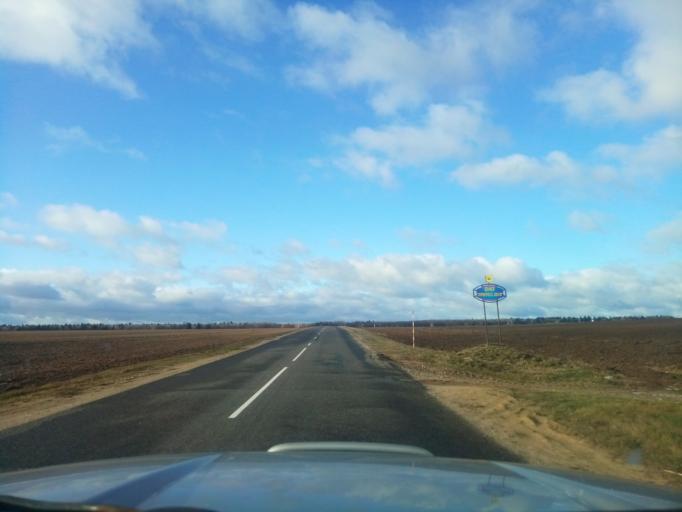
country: BY
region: Minsk
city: Kapyl'
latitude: 53.1695
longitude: 27.0469
